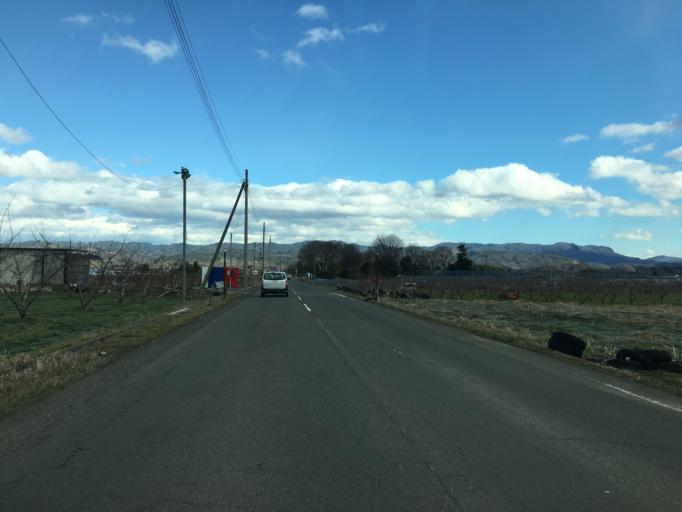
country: JP
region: Fukushima
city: Yanagawamachi-saiwaicho
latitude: 37.8585
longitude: 140.5747
